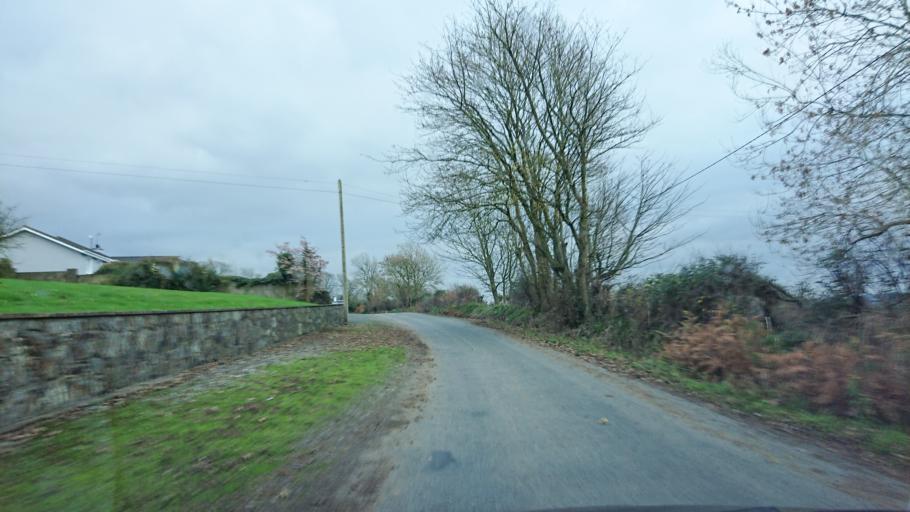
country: IE
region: Munster
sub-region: Waterford
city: Waterford
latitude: 52.2520
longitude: -7.0109
